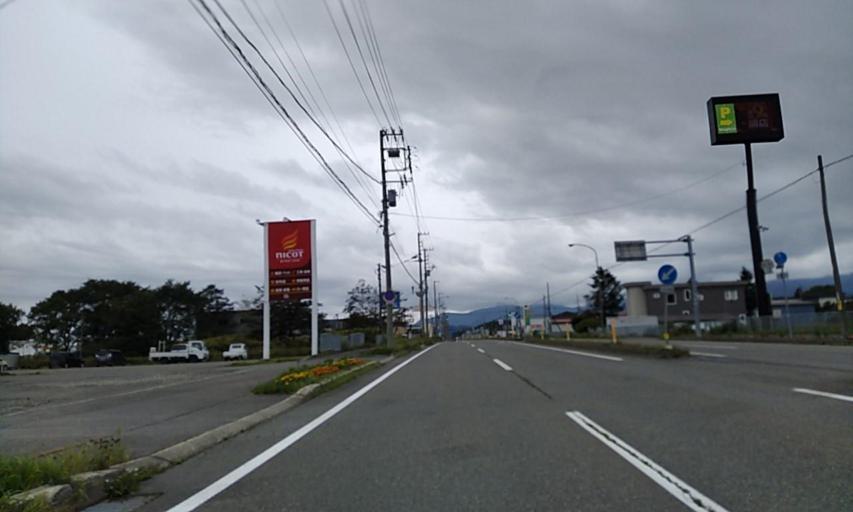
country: JP
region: Hokkaido
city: Obihiro
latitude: 42.3069
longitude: 143.3189
